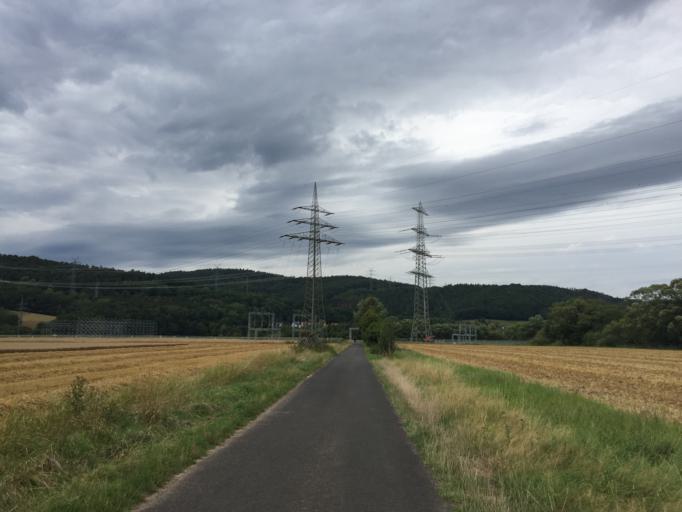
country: DE
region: Hesse
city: Breitenbach
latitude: 50.9132
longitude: 9.7525
